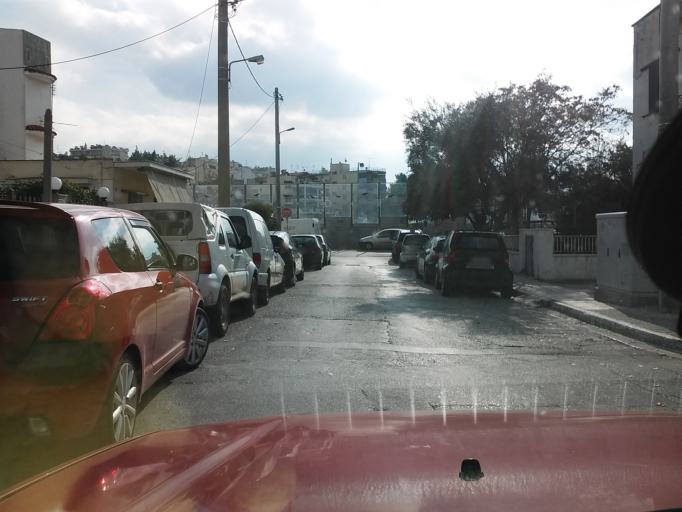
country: GR
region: Attica
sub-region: Nomarchia Athinas
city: Metamorfosi
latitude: 38.0607
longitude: 23.7588
